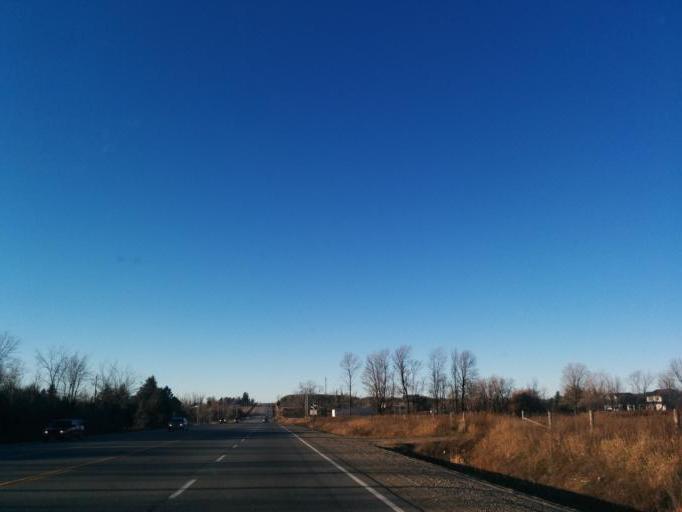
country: CA
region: Ontario
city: Orangeville
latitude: 43.8711
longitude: -80.0104
